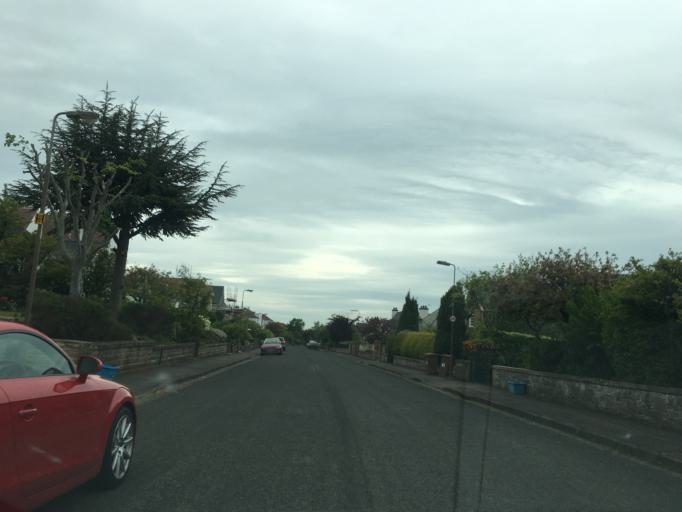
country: GB
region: Scotland
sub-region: Edinburgh
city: Edinburgh
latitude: 55.9178
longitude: -3.2044
